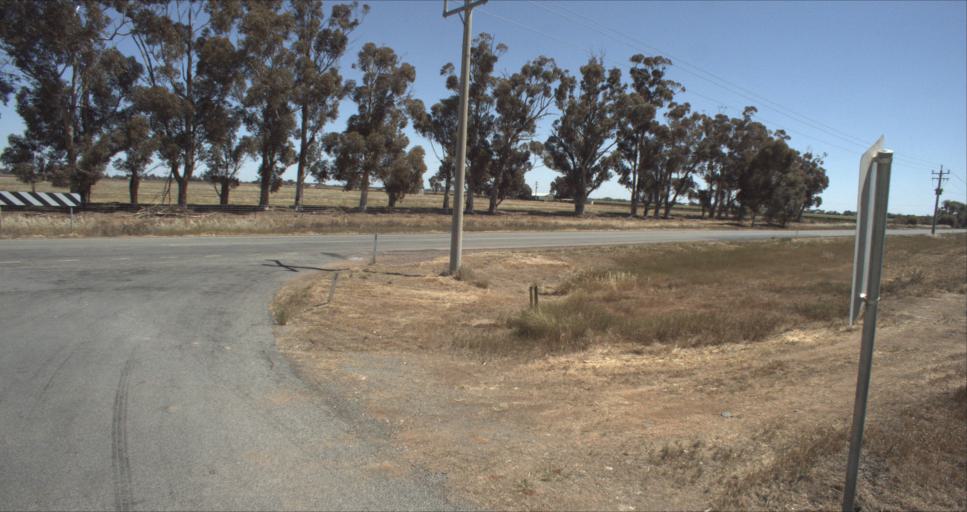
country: AU
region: New South Wales
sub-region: Leeton
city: Leeton
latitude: -34.5024
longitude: 146.4112
